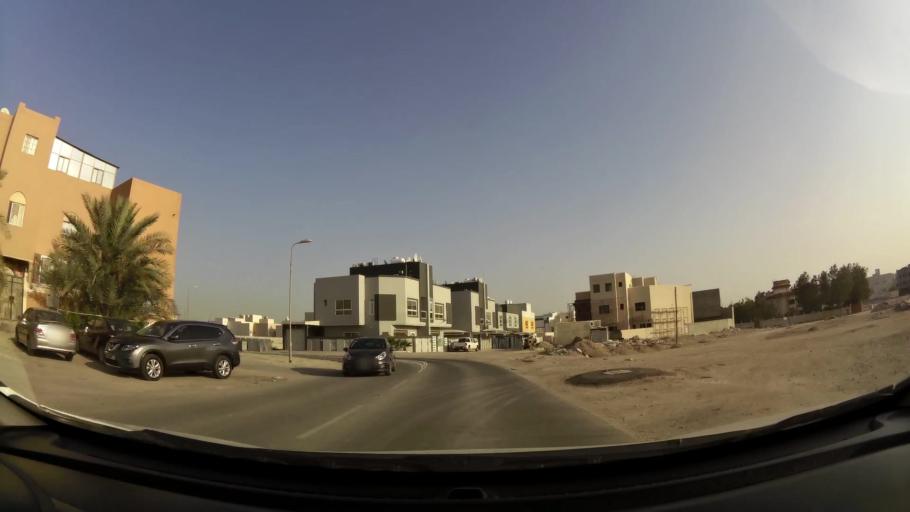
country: BH
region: Manama
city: Jidd Hafs
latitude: 26.2103
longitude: 50.5023
